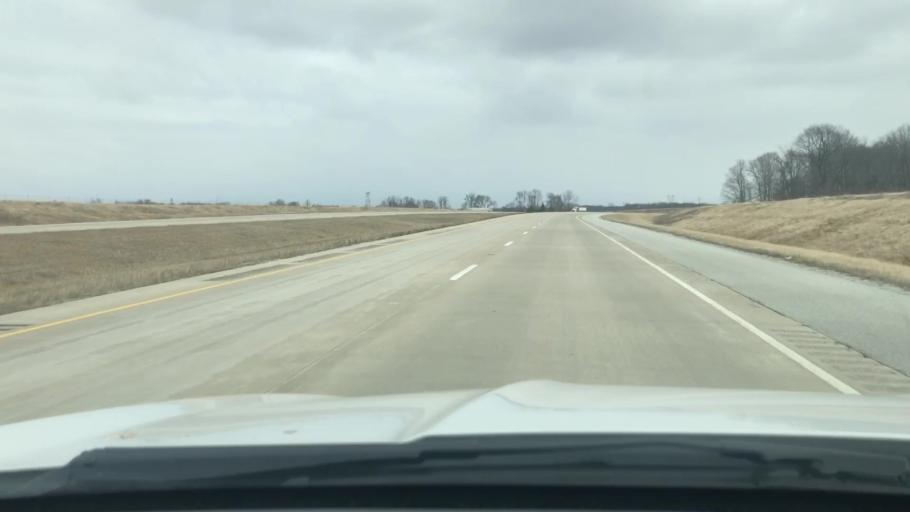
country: US
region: Indiana
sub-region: Carroll County
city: Delphi
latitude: 40.6208
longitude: -86.6282
